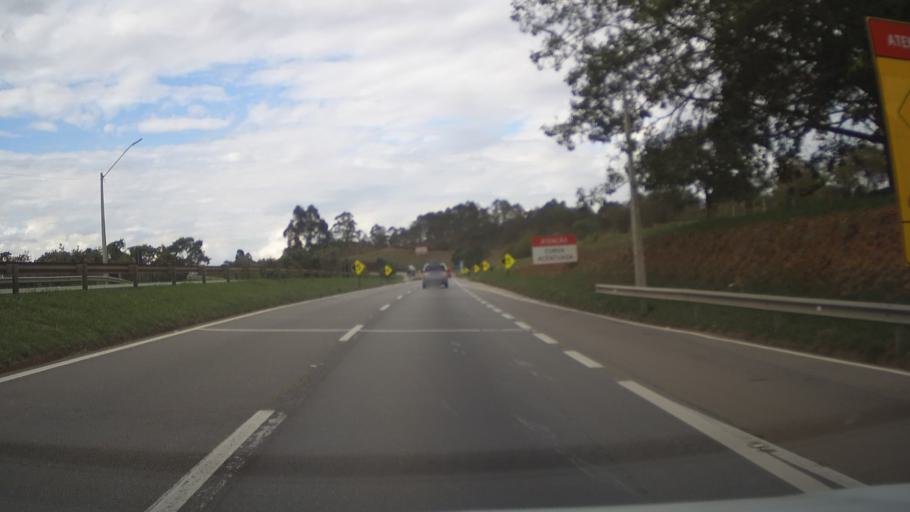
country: BR
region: Minas Gerais
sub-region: Itauna
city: Itauna
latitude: -20.3030
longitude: -44.4447
